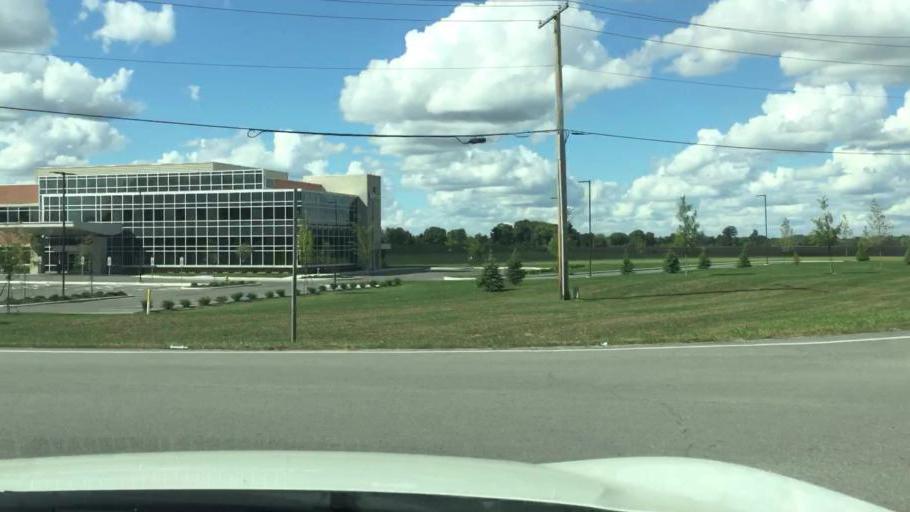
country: US
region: Ohio
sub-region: Champaign County
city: Urbana
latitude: 40.1067
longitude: -83.7124
